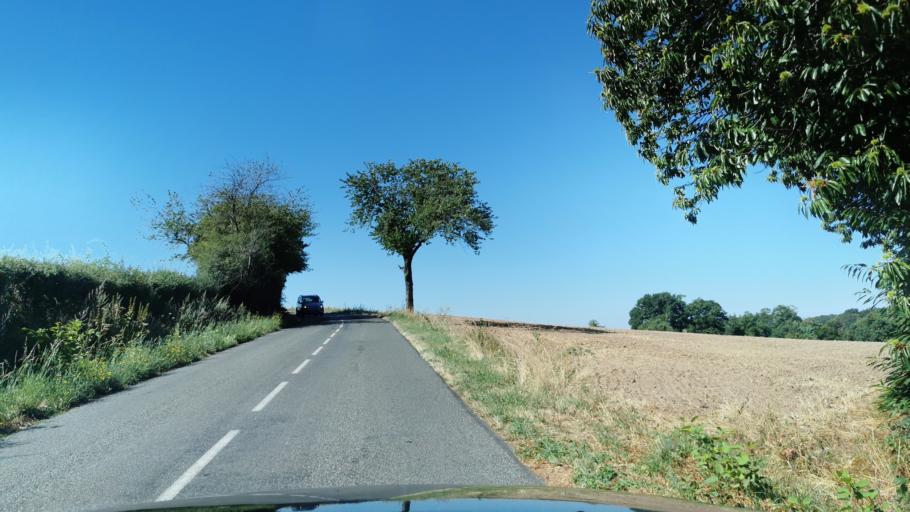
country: FR
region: Bourgogne
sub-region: Departement de Saone-et-Loire
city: Le Breuil
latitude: 46.7878
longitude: 4.4825
